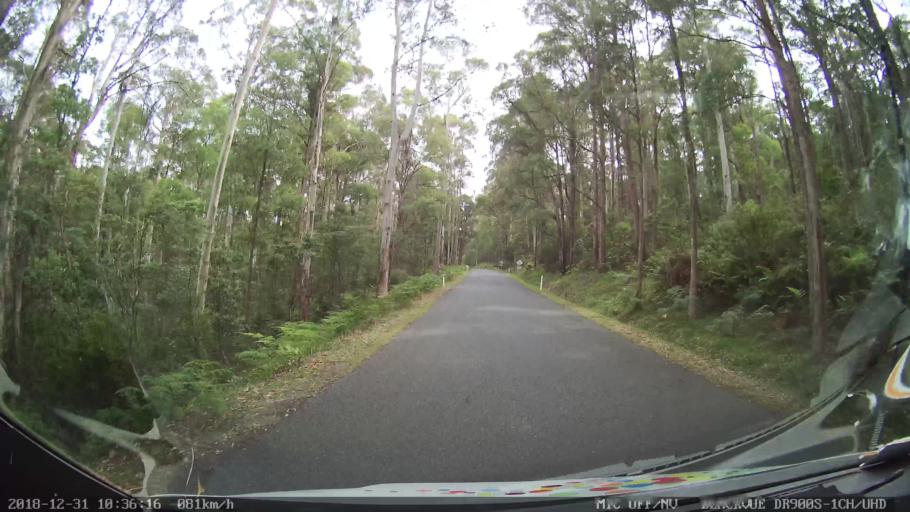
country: AU
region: New South Wales
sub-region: Snowy River
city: Jindabyne
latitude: -36.4280
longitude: 148.1708
